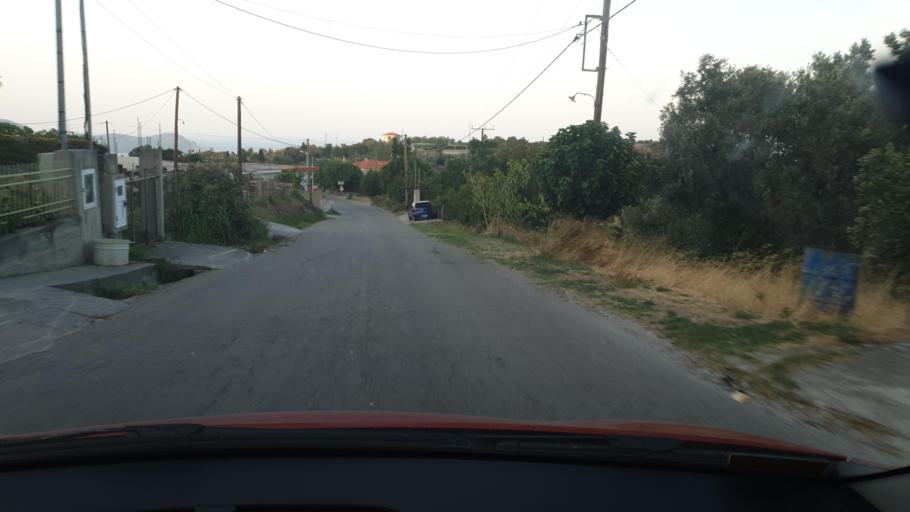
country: GR
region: Central Greece
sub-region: Nomos Evvoias
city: Oxilithos
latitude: 38.5870
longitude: 24.1133
